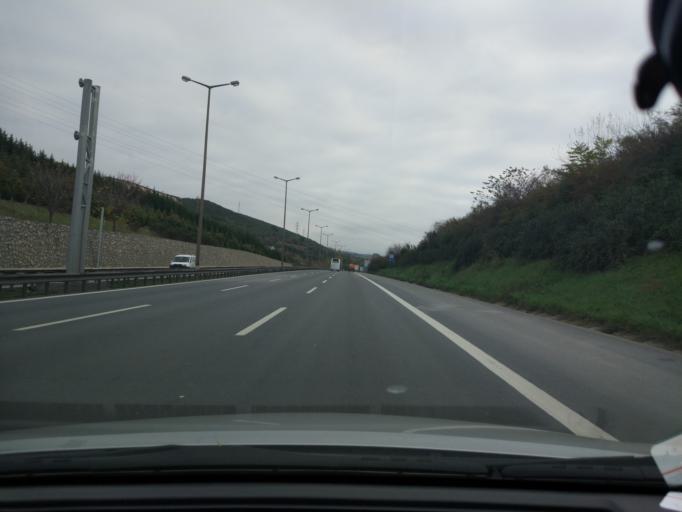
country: TR
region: Kocaeli
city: Izmit
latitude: 40.7697
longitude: 29.8683
